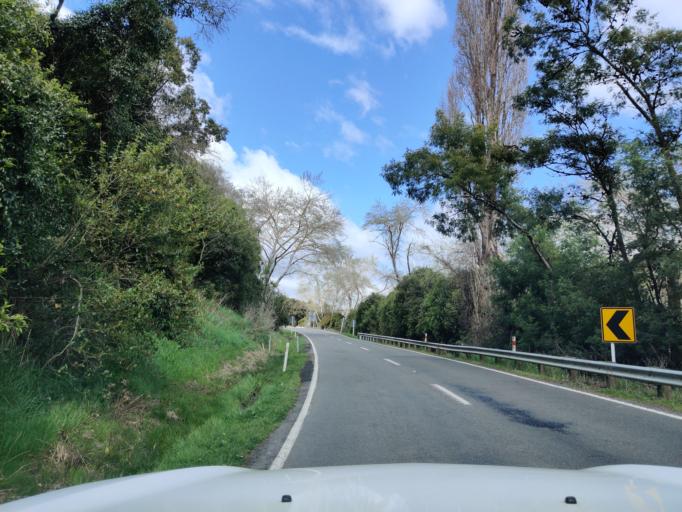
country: NZ
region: Manawatu-Wanganui
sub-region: Ruapehu District
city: Waiouru
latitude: -39.6479
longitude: 175.3242
